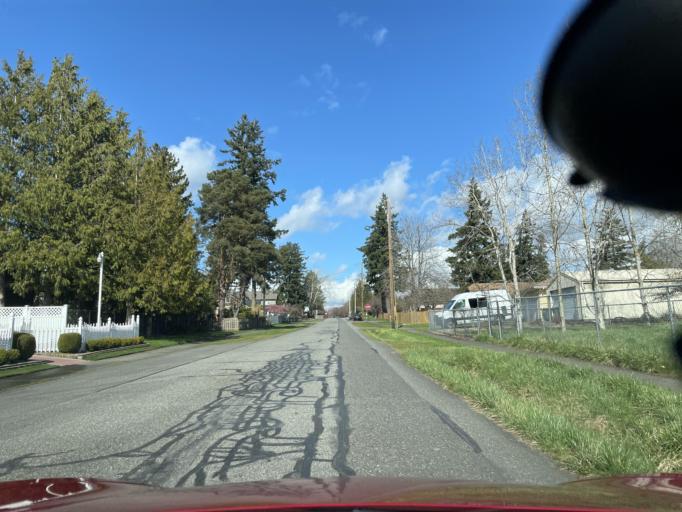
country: US
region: Washington
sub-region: Whatcom County
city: Bellingham
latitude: 48.7660
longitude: -122.4562
